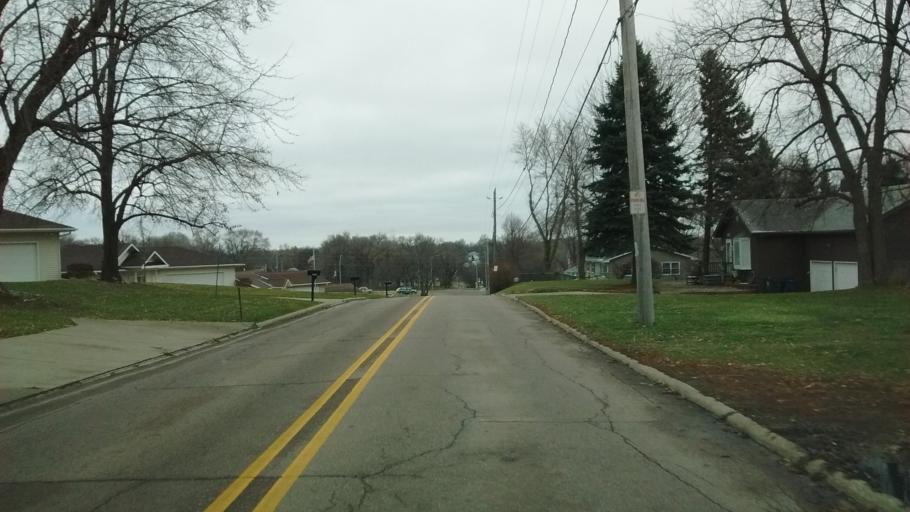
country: US
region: Iowa
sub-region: Woodbury County
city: Sioux City
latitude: 42.4781
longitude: -96.3396
